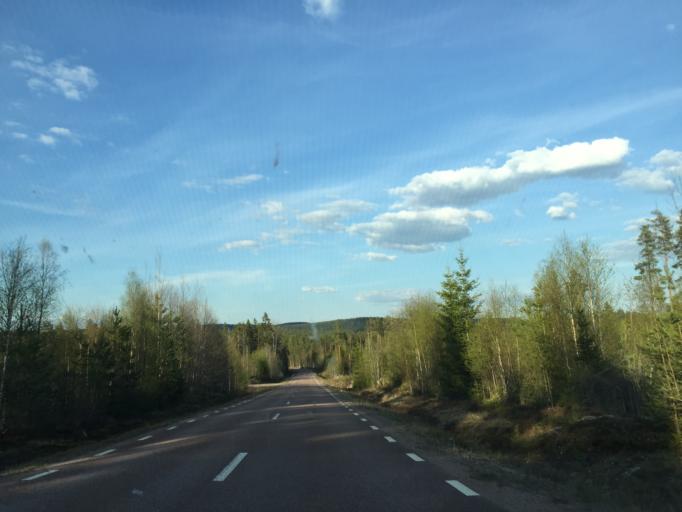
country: SE
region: Dalarna
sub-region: Leksand Municipality
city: Siljansnas
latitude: 60.6791
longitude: 14.7217
